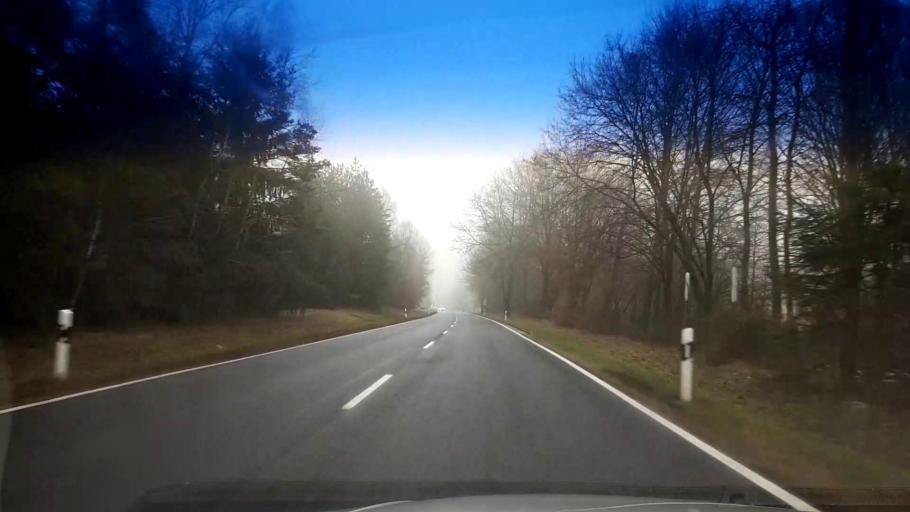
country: DE
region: Bavaria
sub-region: Upper Palatinate
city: Berg
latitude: 49.8573
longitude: 12.1710
